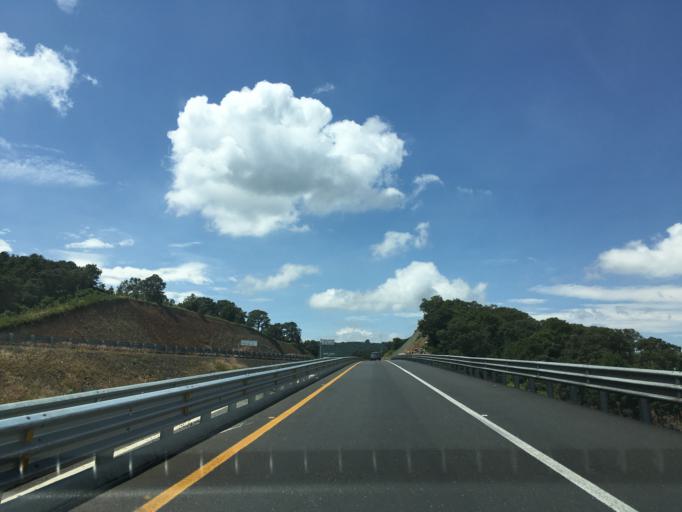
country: MX
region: Michoacan
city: Patzcuaro
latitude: 19.5269
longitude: -101.5666
